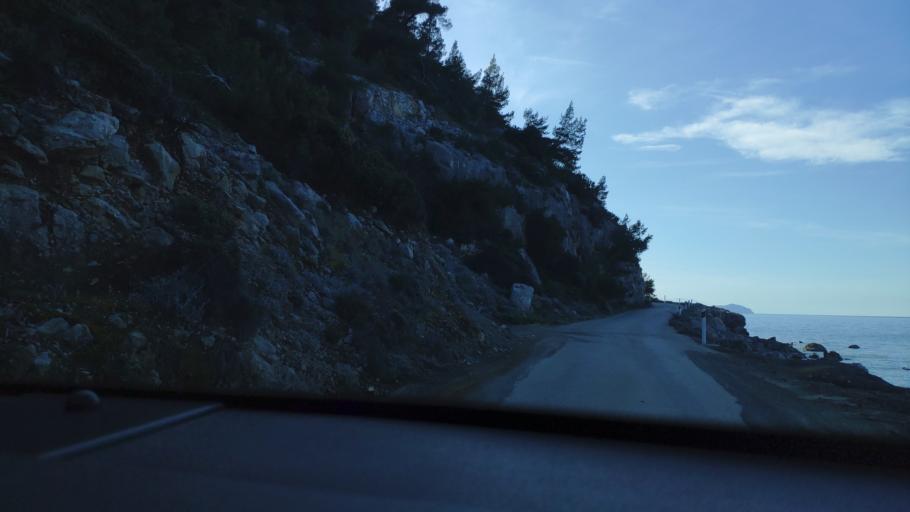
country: GR
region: Attica
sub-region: Nomarchia Dytikis Attikis
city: Kineta
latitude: 38.0638
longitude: 23.1273
